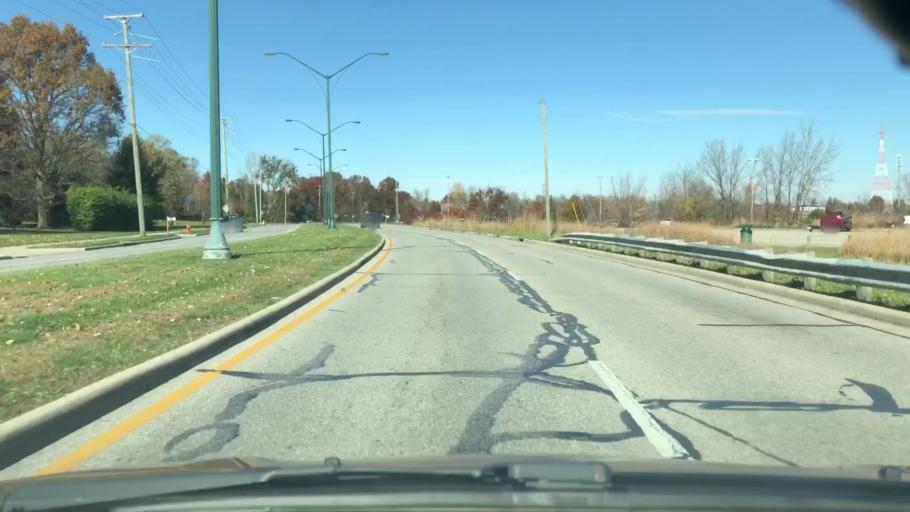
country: US
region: Ohio
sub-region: Franklin County
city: Westerville
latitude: 40.1212
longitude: -82.8859
